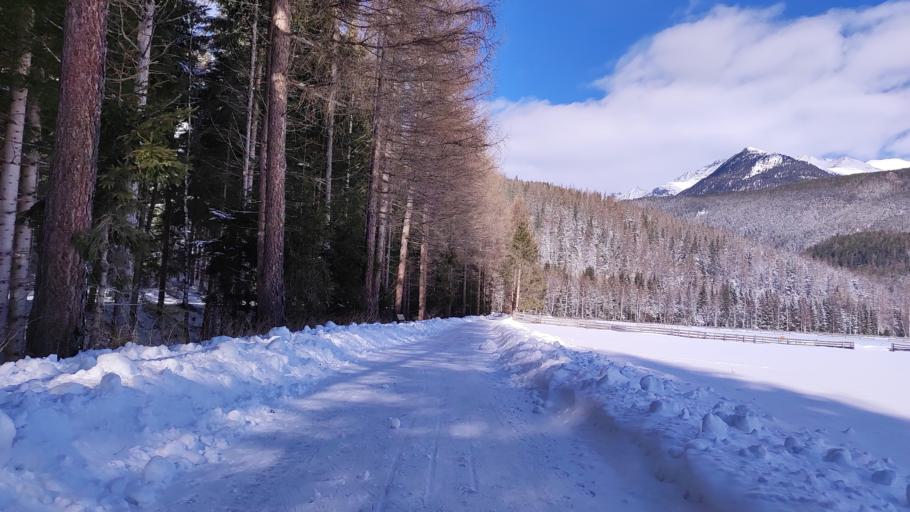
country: AT
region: Tyrol
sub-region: Politischer Bezirk Imst
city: Umhausen
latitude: 47.0989
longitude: 10.9372
